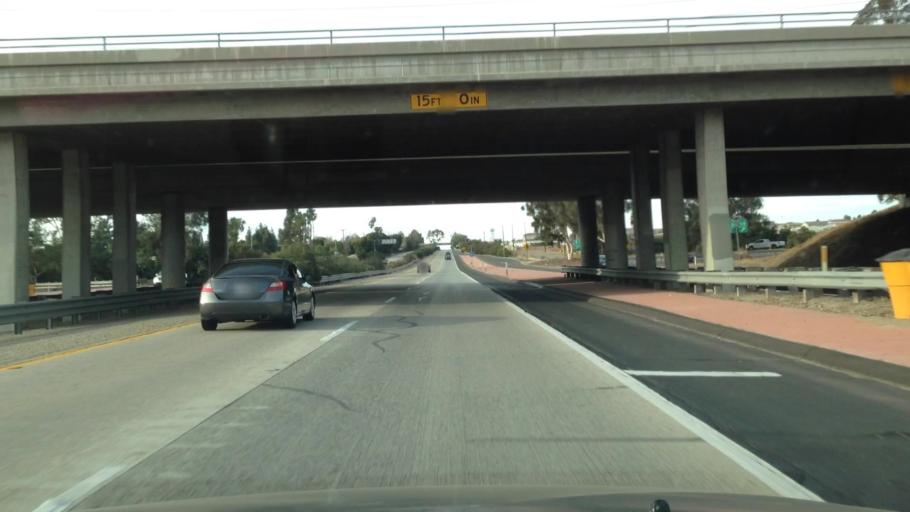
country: US
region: California
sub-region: Ventura County
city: Saticoy
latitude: 34.2900
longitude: -119.1561
